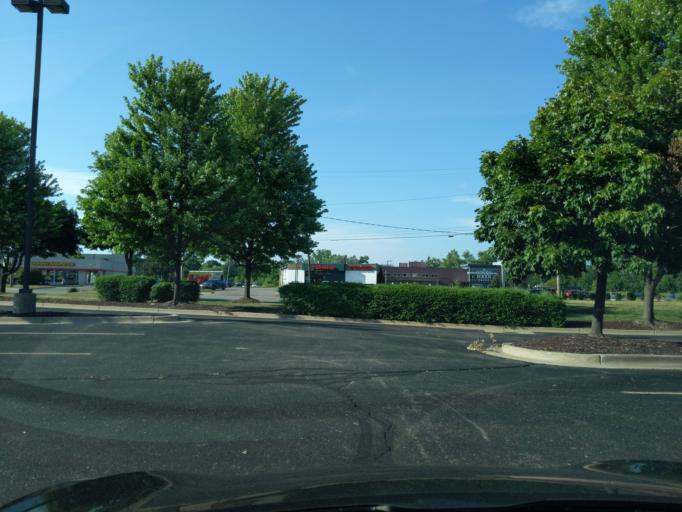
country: US
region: Michigan
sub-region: Ingham County
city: Okemos
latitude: 42.7265
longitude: -84.4536
